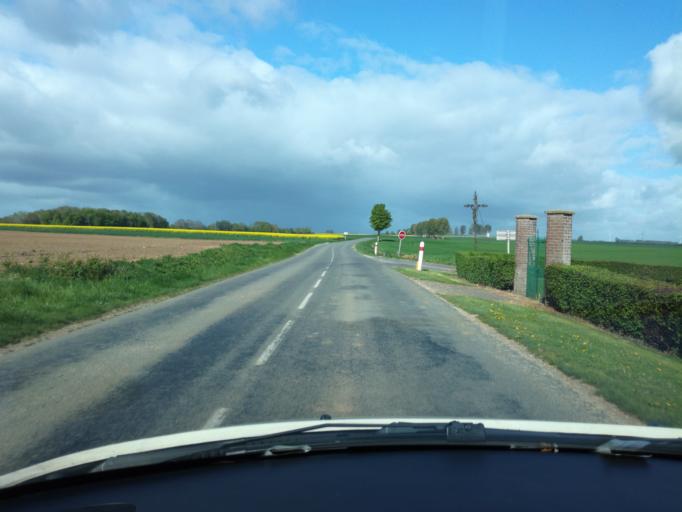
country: FR
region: Picardie
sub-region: Departement de la Somme
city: Hornoy-le-Bourg
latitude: 49.8529
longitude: 1.8733
